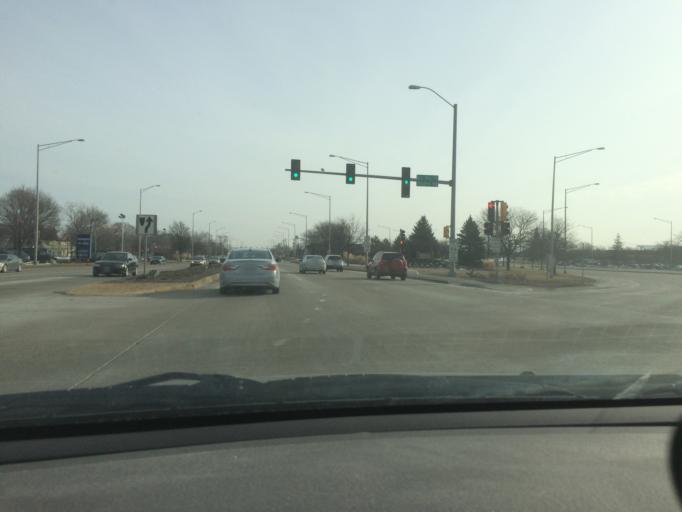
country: US
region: Illinois
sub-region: Cook County
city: Hoffman Estates
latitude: 42.0485
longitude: -88.0959
